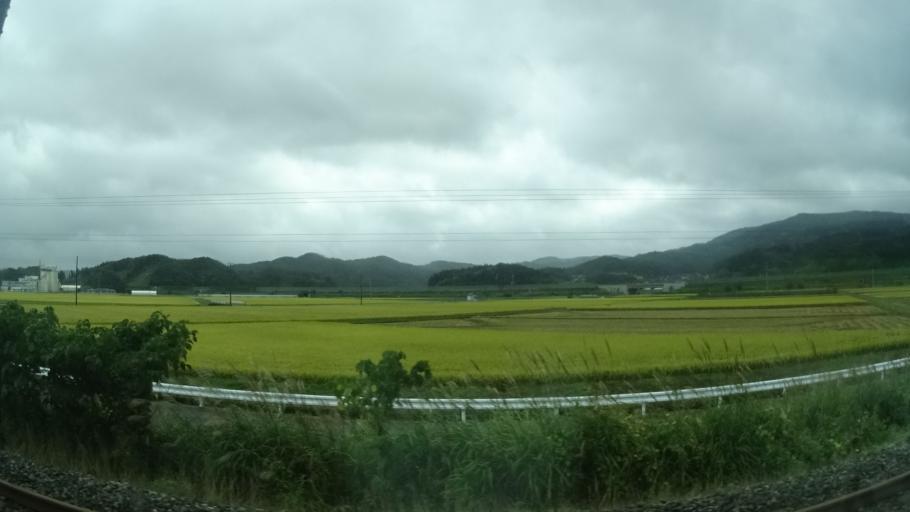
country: JP
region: Yamagata
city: Tsuruoka
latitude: 38.7095
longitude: 139.7248
